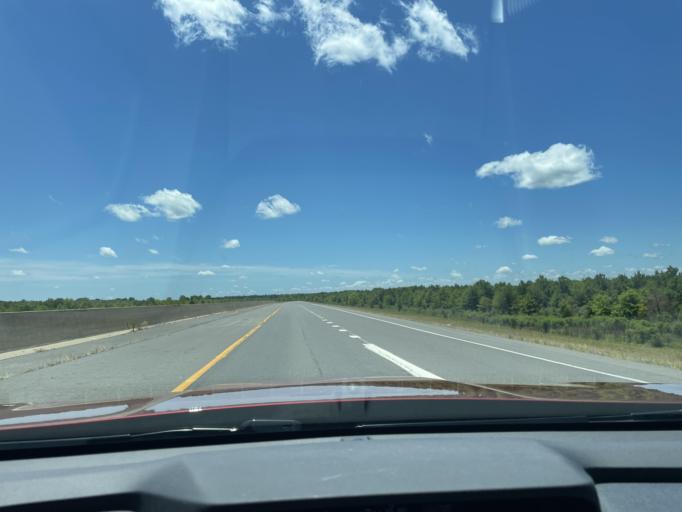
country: US
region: Arkansas
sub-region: Jefferson County
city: Pine Bluff
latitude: 34.1679
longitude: -91.9858
